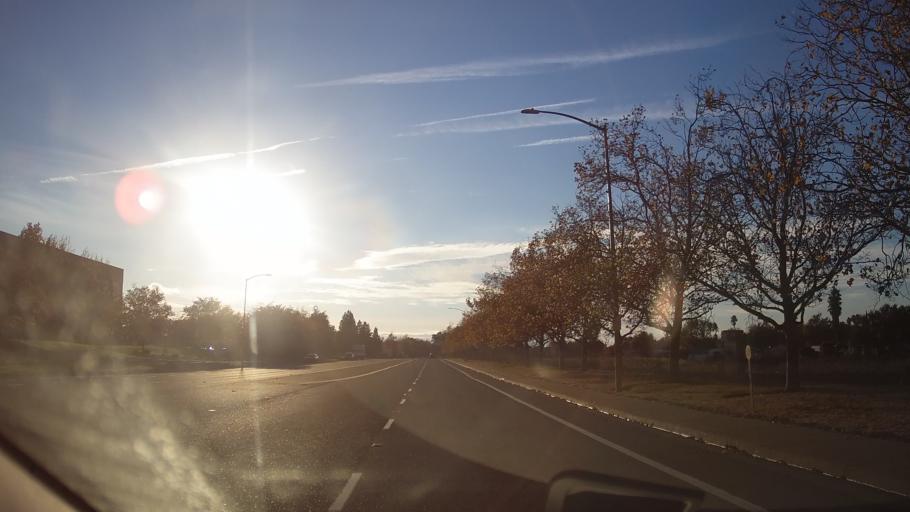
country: US
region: California
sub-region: Yolo County
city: West Sacramento
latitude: 38.5722
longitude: -121.5691
